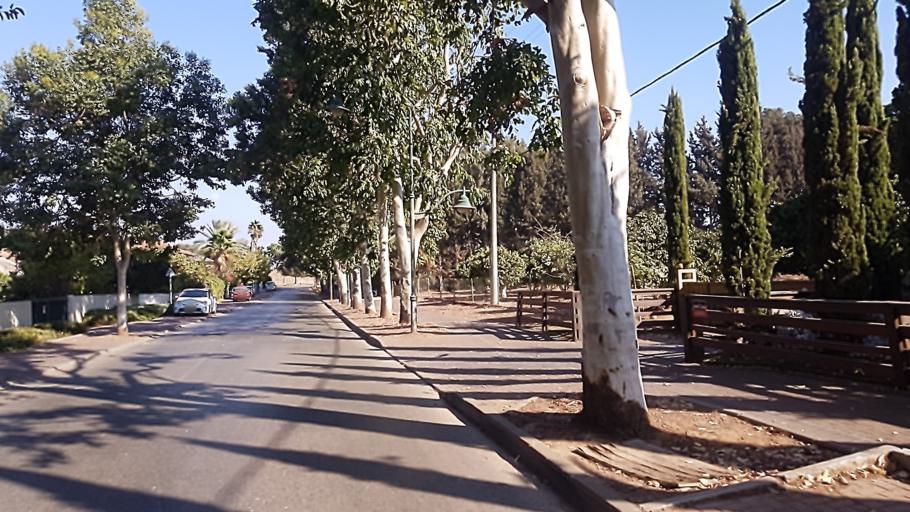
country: IL
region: Central District
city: Kfar Saba
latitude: 32.2098
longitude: 34.9024
